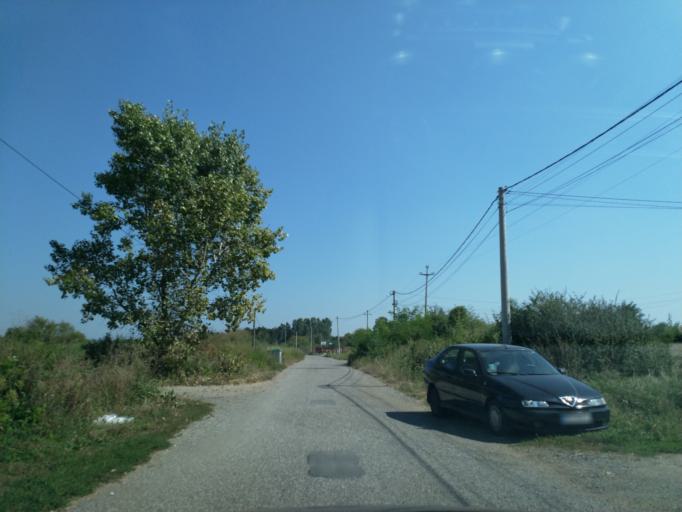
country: RS
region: Central Serbia
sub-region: Rasinski Okrug
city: Trstenik
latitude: 43.6120
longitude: 21.0266
